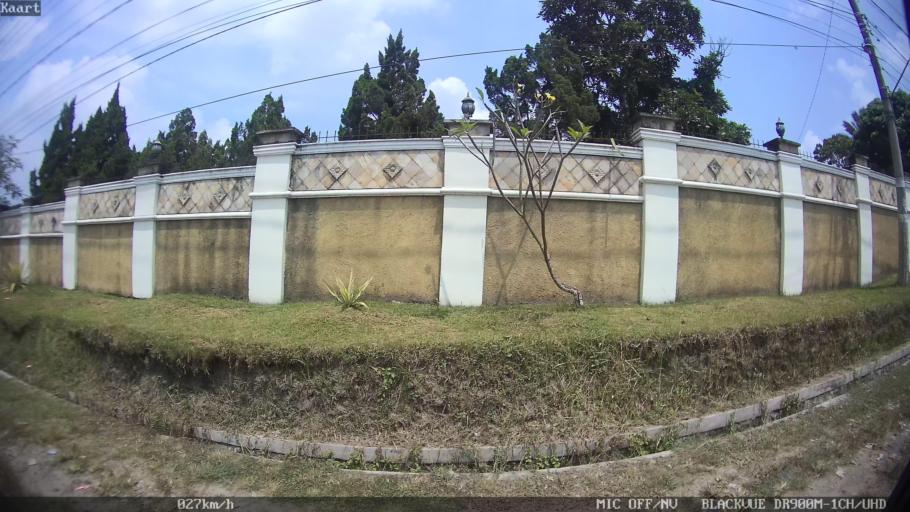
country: ID
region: Lampung
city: Pringsewu
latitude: -5.3406
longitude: 104.9750
